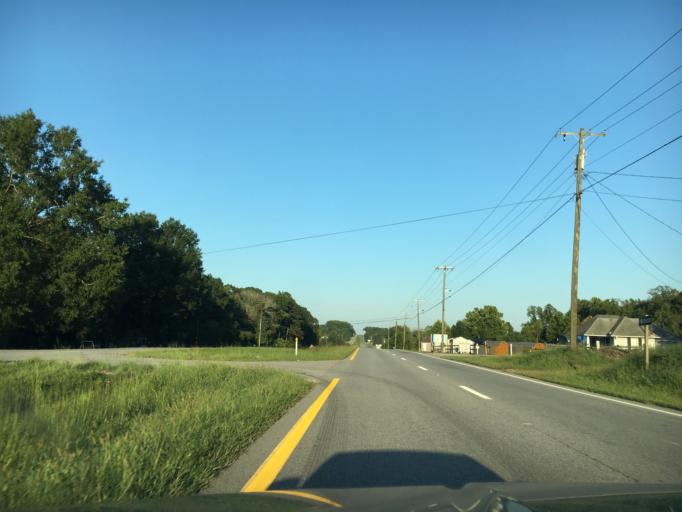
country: US
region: Virginia
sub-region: City of Danville
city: Danville
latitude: 36.5808
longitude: -79.2985
